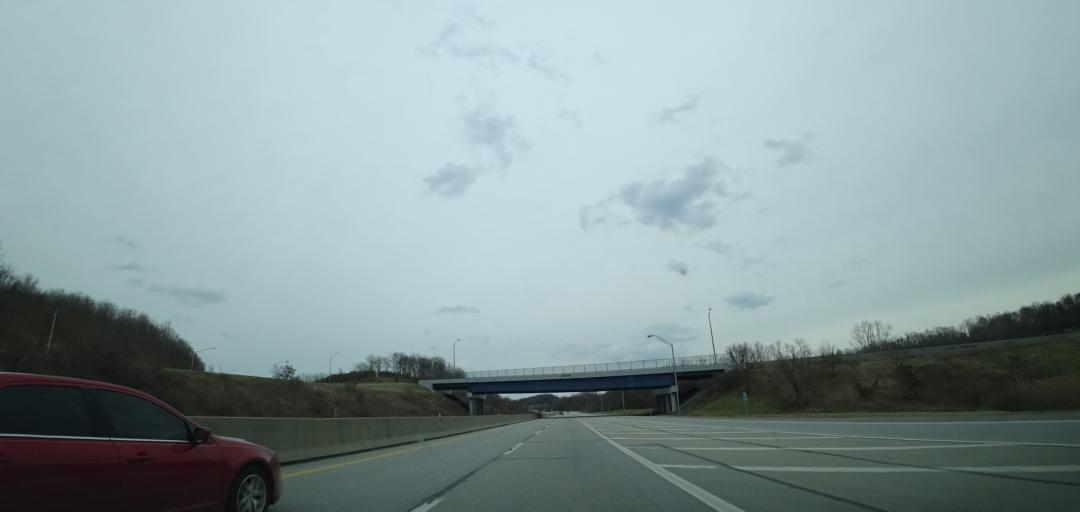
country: US
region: Pennsylvania
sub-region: Beaver County
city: Big Beaver
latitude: 40.8381
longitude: -80.3804
